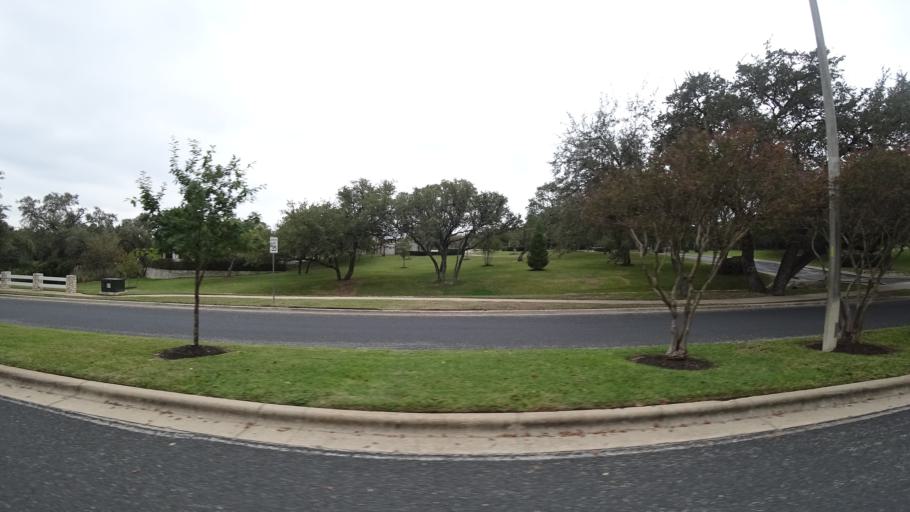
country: US
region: Texas
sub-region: Williamson County
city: Anderson Mill
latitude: 30.4408
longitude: -97.8270
